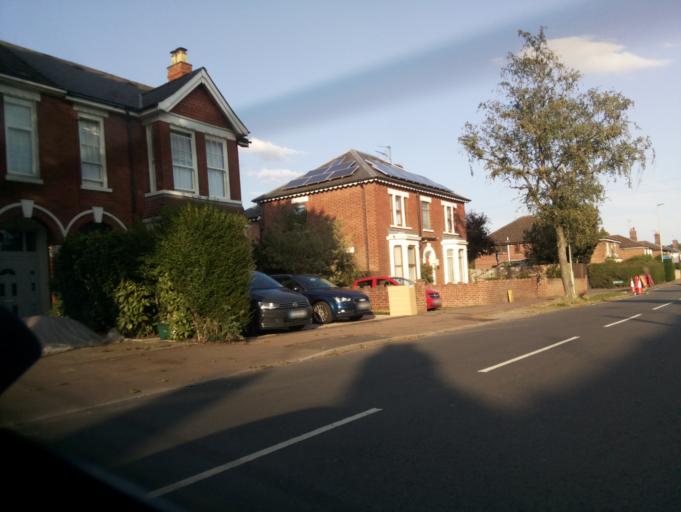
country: GB
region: England
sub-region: Gloucestershire
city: Gloucester
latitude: 51.8482
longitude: -2.2550
